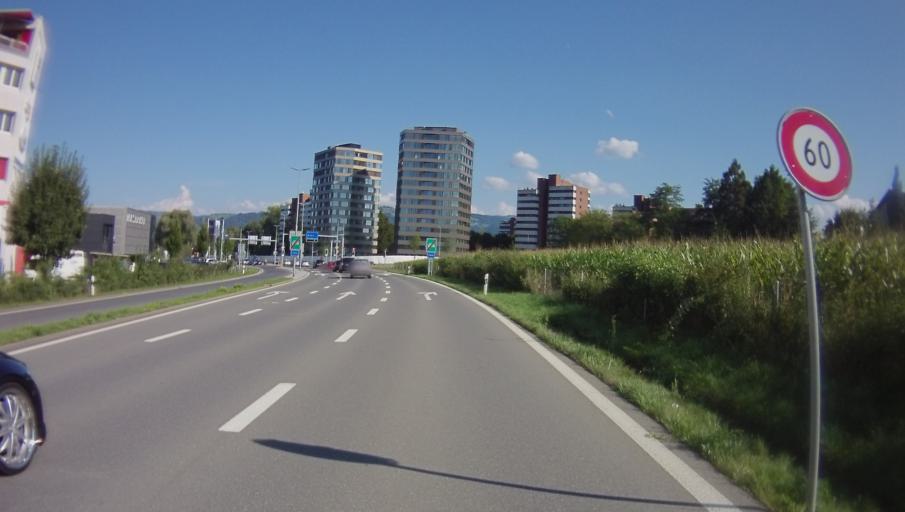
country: CH
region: Zug
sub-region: Zug
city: Cham
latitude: 47.1865
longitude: 8.4723
